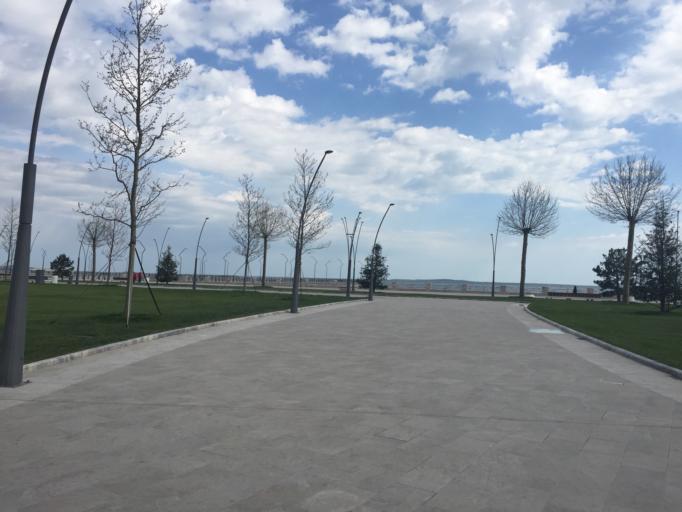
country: AZ
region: Baki
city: Baku
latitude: 40.3747
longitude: 49.8798
